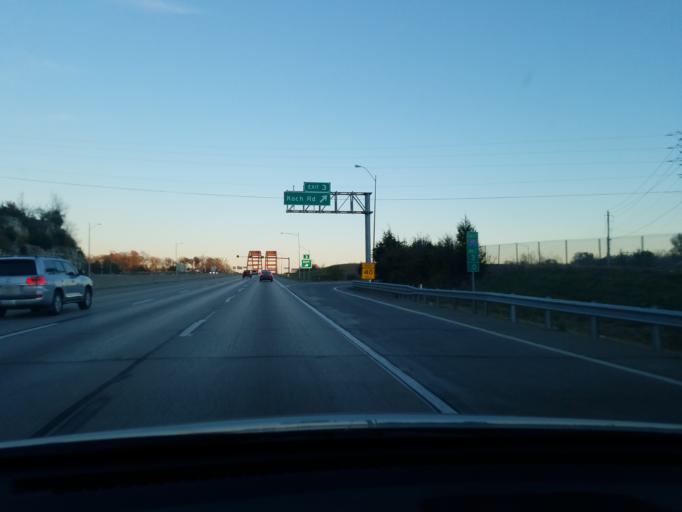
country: US
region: Missouri
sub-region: Saint Louis County
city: Oakville
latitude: 38.4901
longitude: -90.2882
